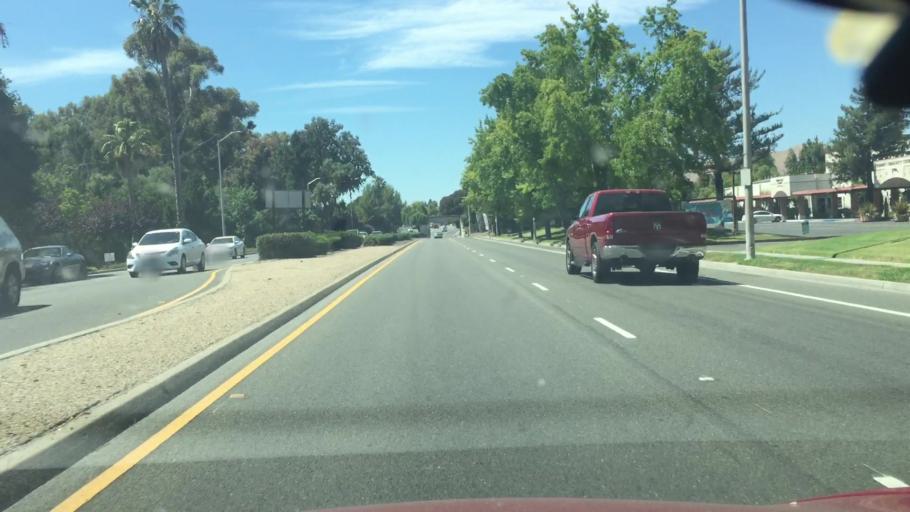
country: US
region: California
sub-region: Alameda County
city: Fremont
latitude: 37.5584
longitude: -121.9533
